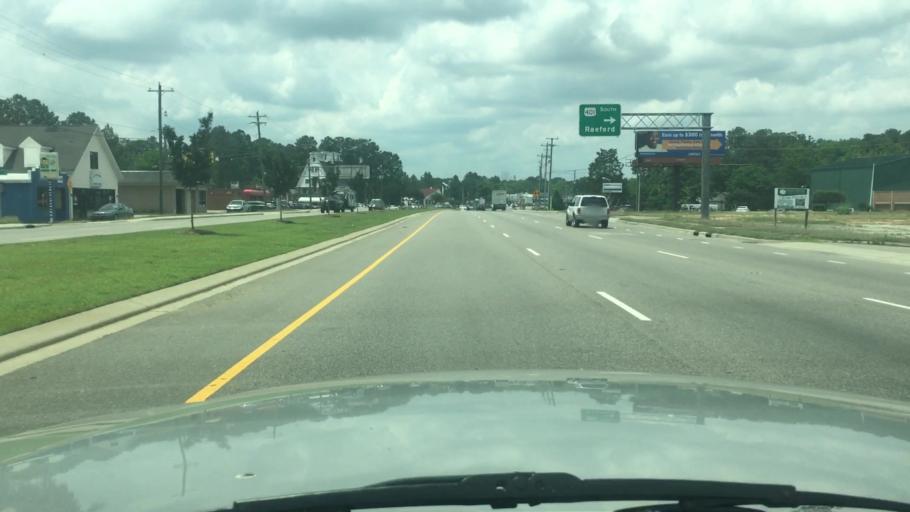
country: US
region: North Carolina
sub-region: Cumberland County
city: Fort Bragg
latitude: 35.0864
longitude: -78.9506
